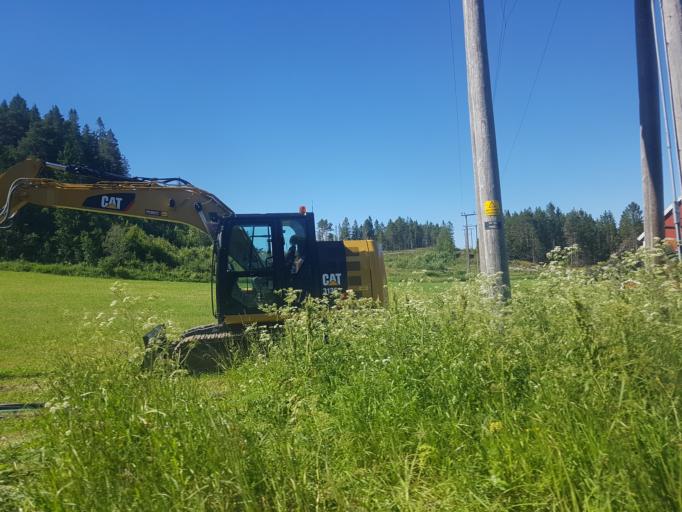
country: NO
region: Sor-Trondelag
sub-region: Skaun
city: Borsa
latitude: 63.4400
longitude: 10.1980
